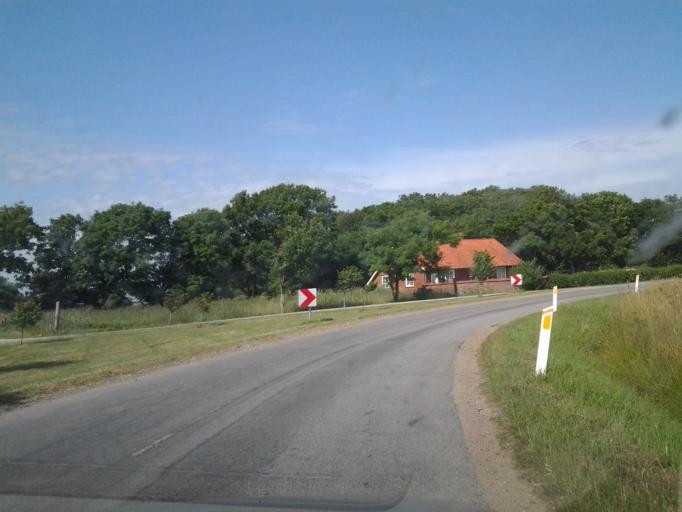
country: DE
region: Schleswig-Holstein
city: Aventoft
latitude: 54.9218
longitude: 8.7866
